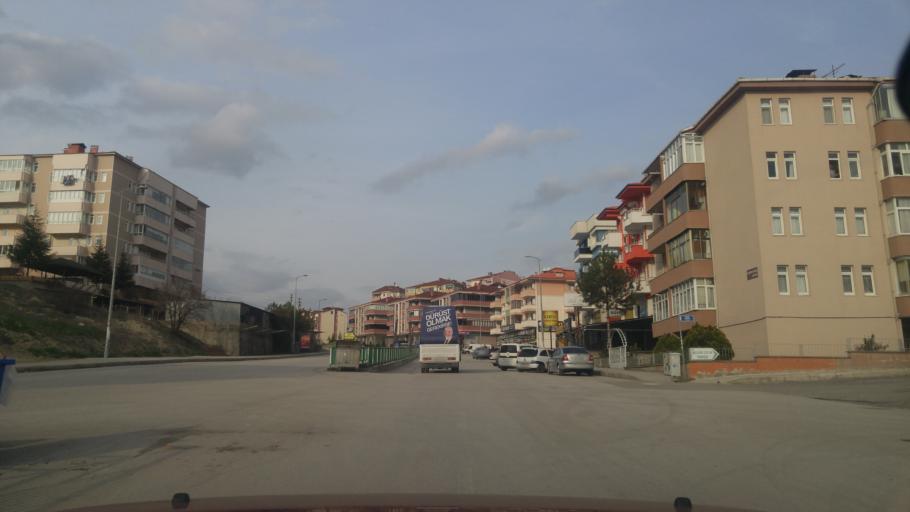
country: TR
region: Karabuk
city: Karabuk
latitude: 41.2215
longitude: 32.6615
